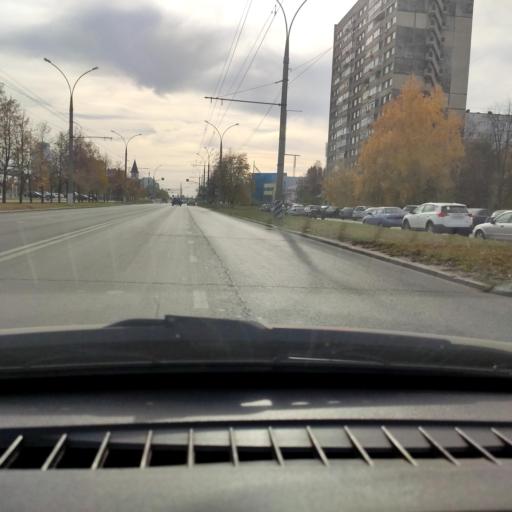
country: RU
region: Samara
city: Tol'yatti
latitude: 53.5091
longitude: 49.2713
